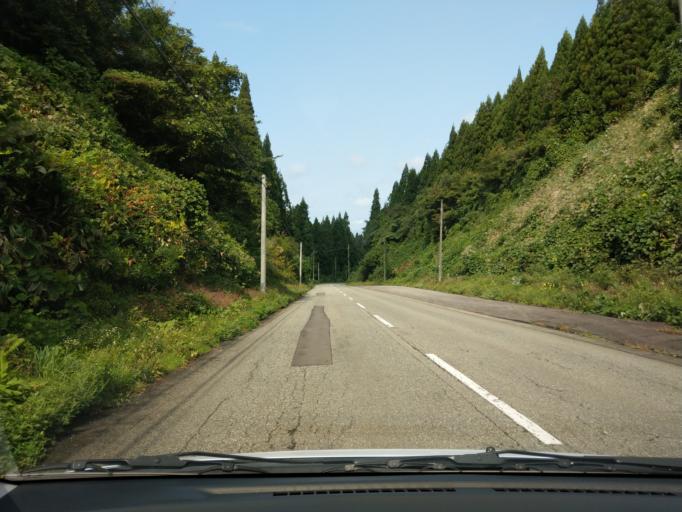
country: JP
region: Akita
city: Omagari
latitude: 39.5118
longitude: 140.3077
